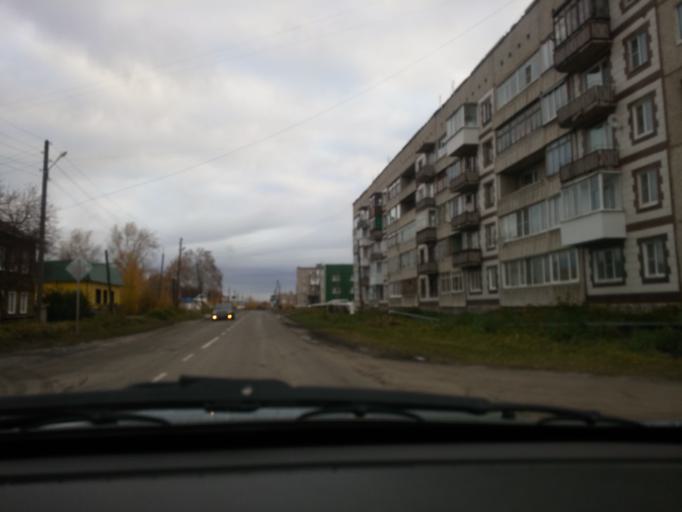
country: RU
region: Sverdlovsk
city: Turinsk
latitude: 58.0388
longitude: 63.7056
